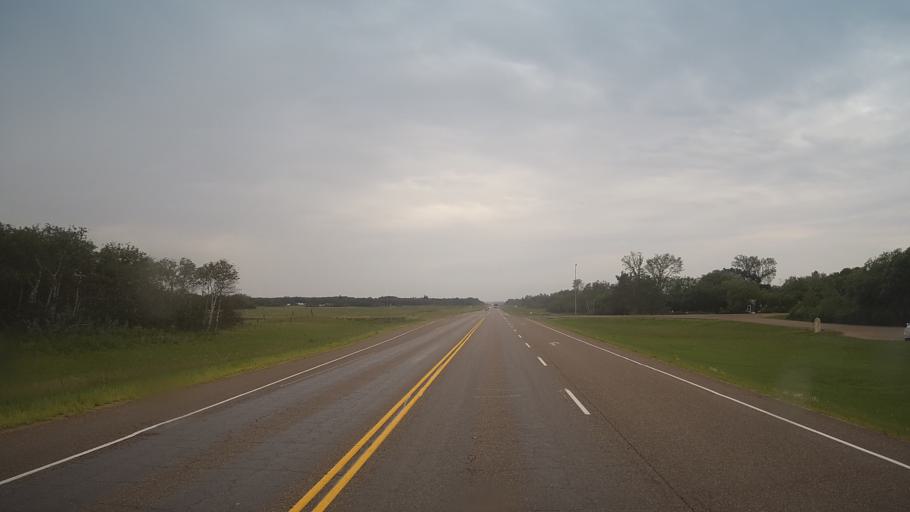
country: CA
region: Saskatchewan
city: Langham
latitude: 52.1293
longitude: -107.0249
